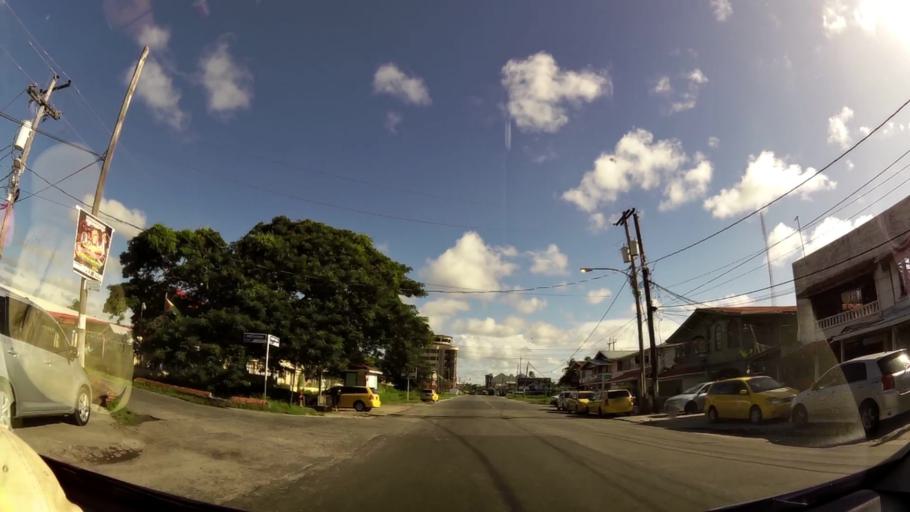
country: GY
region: Demerara-Mahaica
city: Georgetown
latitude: 6.8141
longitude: -58.1362
